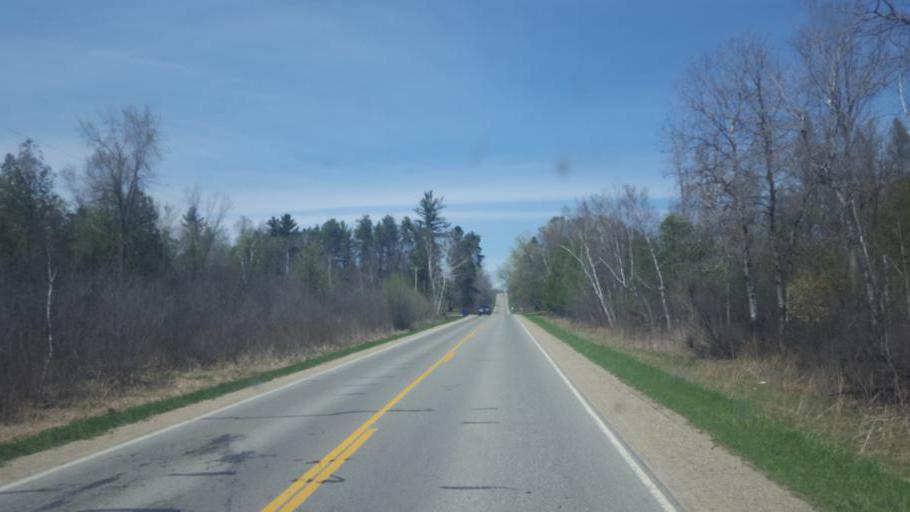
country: US
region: Michigan
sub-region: Gladwin County
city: Beaverton
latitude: 43.9221
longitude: -84.5851
